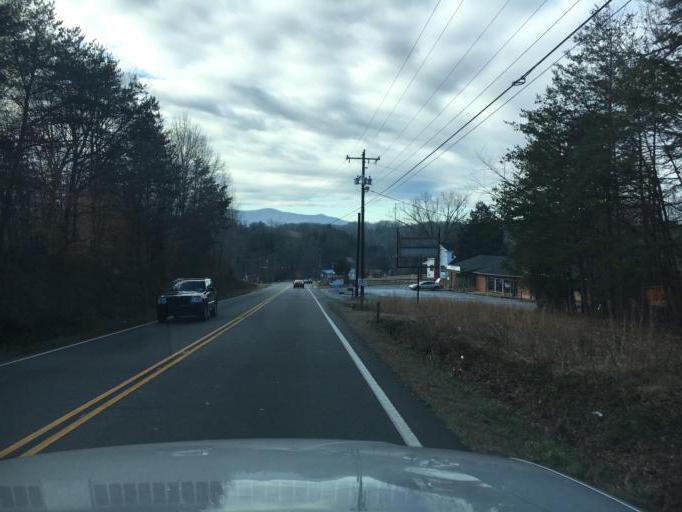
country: US
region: North Carolina
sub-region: Burke County
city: Salem
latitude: 35.7043
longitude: -81.7110
